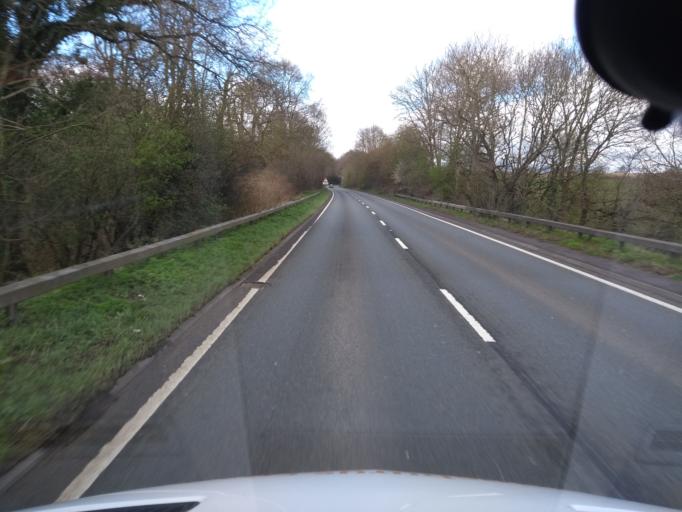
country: GB
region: England
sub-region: Somerset
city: Stoke-sub-Hamdon
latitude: 50.9528
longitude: -2.7049
